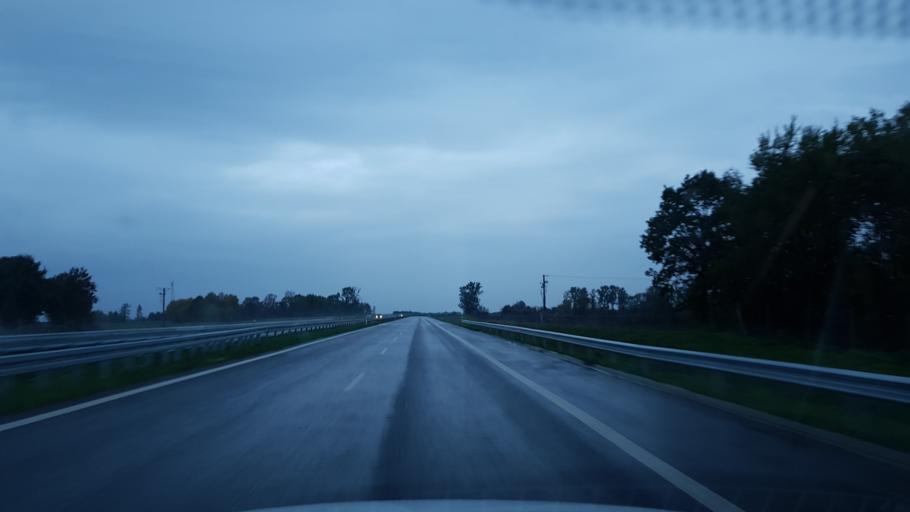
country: PL
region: West Pomeranian Voivodeship
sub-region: Powiat kolobrzeski
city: Ryman
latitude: 54.0163
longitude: 15.4767
